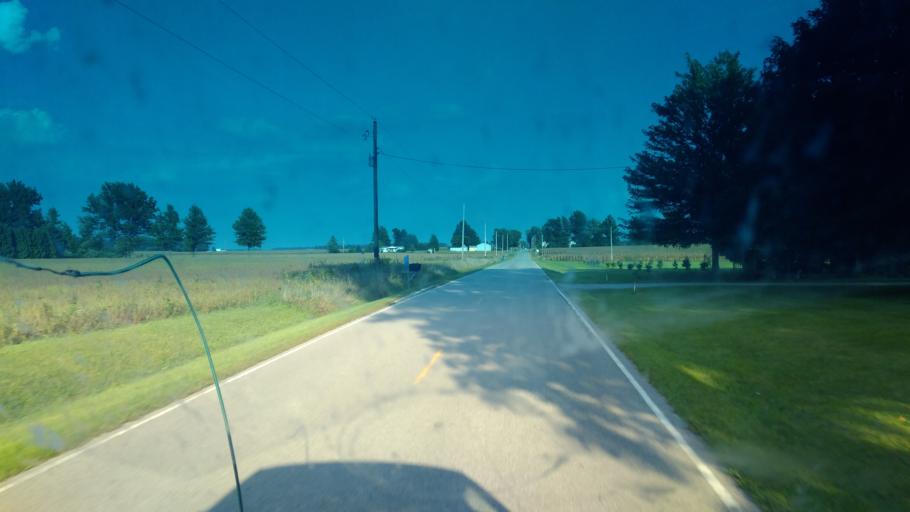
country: US
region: Ohio
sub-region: Crawford County
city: Bucyrus
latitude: 40.9650
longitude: -83.0404
